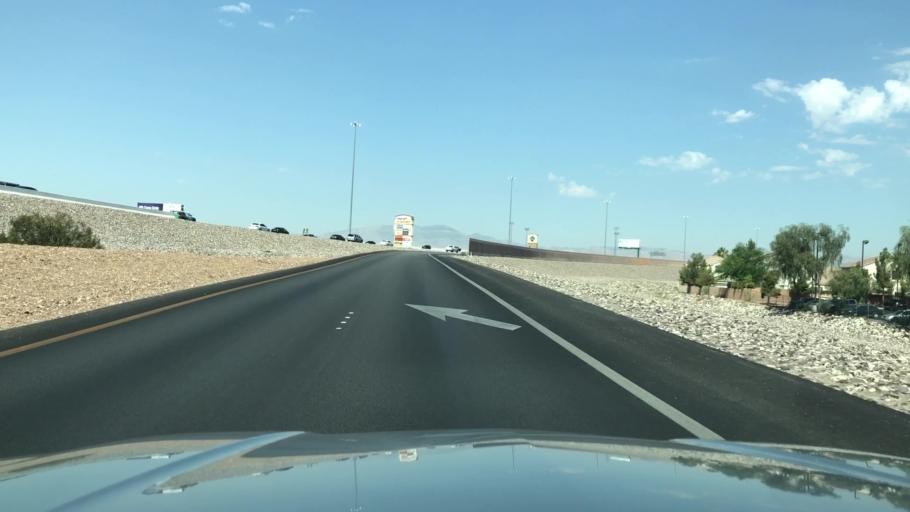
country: US
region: Nevada
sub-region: Clark County
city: Whitney
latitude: 36.0244
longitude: -115.1201
